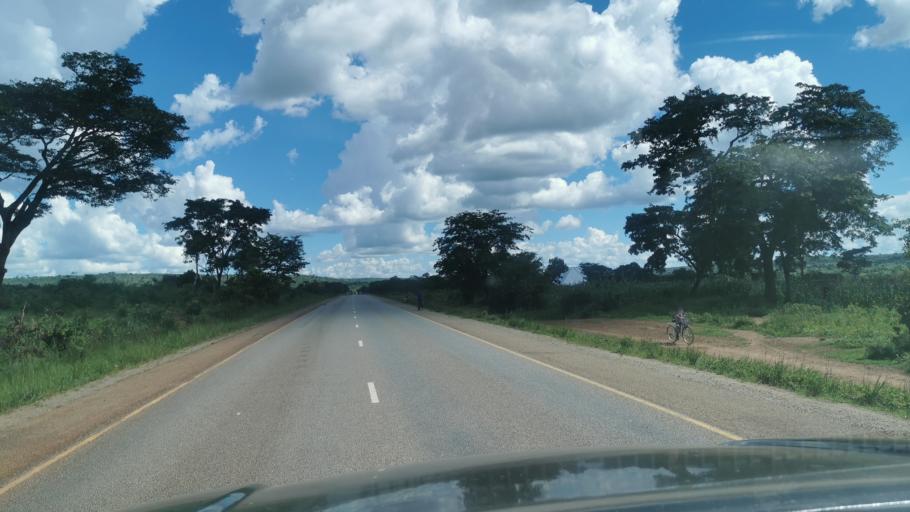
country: TZ
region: Geita
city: Uyovu
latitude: -3.0925
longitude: 31.2971
